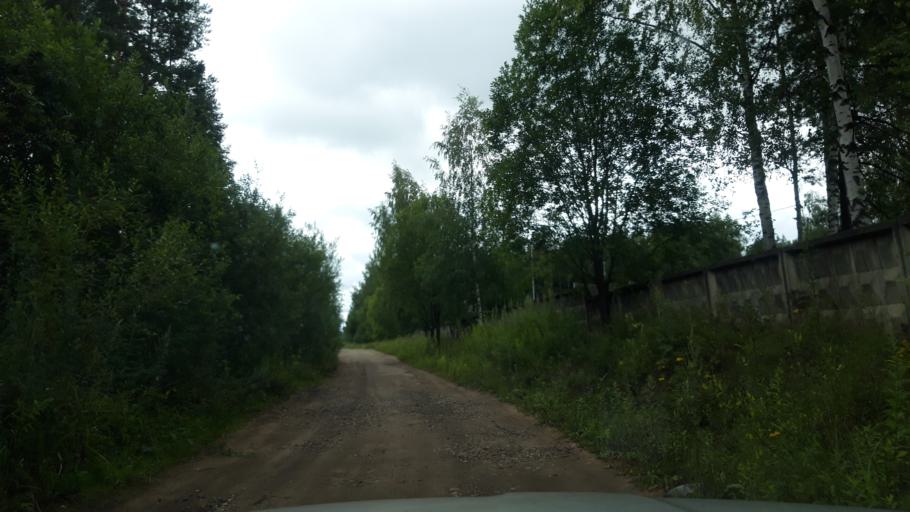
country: RU
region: Moskovskaya
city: Povarovo
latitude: 56.0555
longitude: 37.0582
